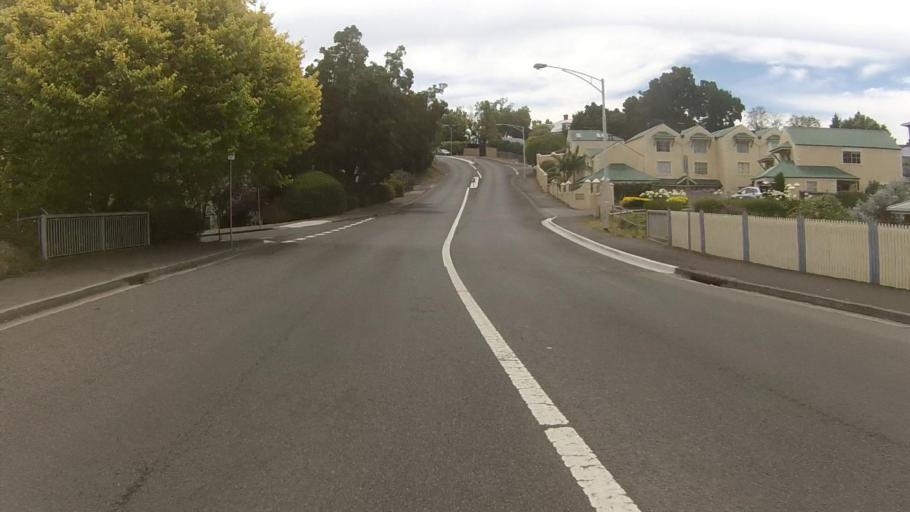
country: AU
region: Tasmania
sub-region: Hobart
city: Sandy Bay
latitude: -42.8936
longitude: 147.3226
